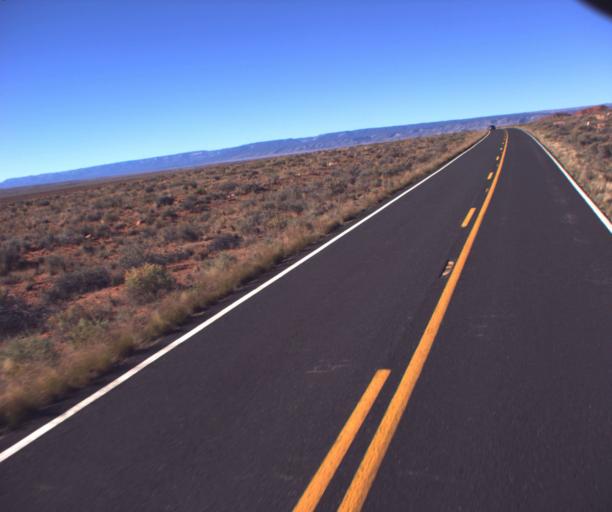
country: US
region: Arizona
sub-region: Coconino County
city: LeChee
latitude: 36.6973
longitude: -111.8062
